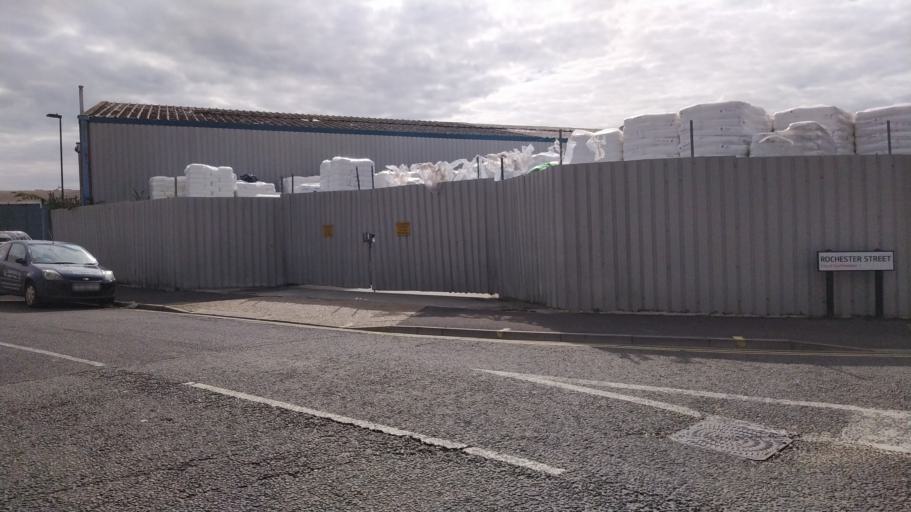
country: GB
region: England
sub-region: Southampton
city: Southampton
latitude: 50.9081
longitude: -1.3901
